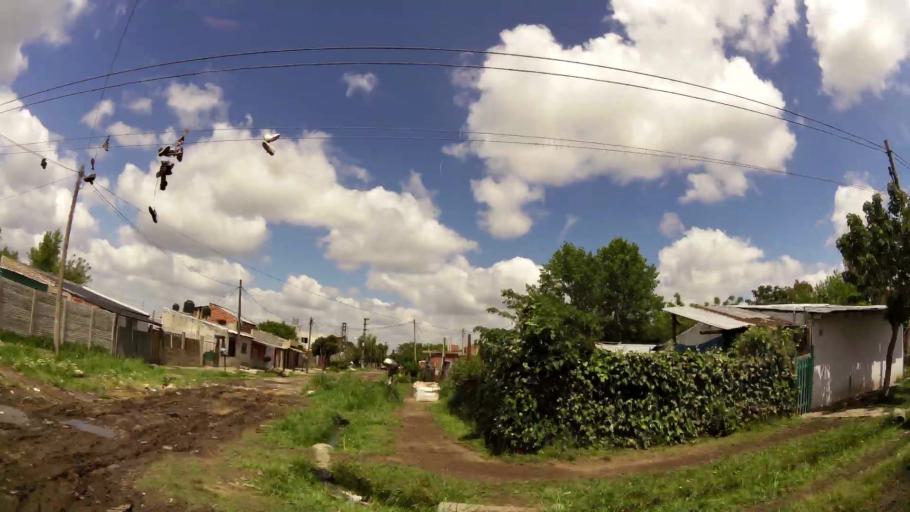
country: AR
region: Buenos Aires
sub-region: Partido de Quilmes
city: Quilmes
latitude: -34.8388
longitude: -58.2289
